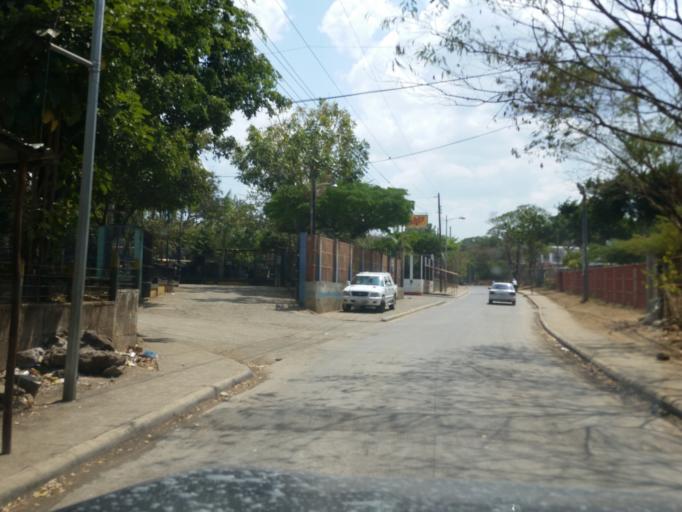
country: NI
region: Masaya
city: Ticuantepe
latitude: 12.0697
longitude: -86.1995
